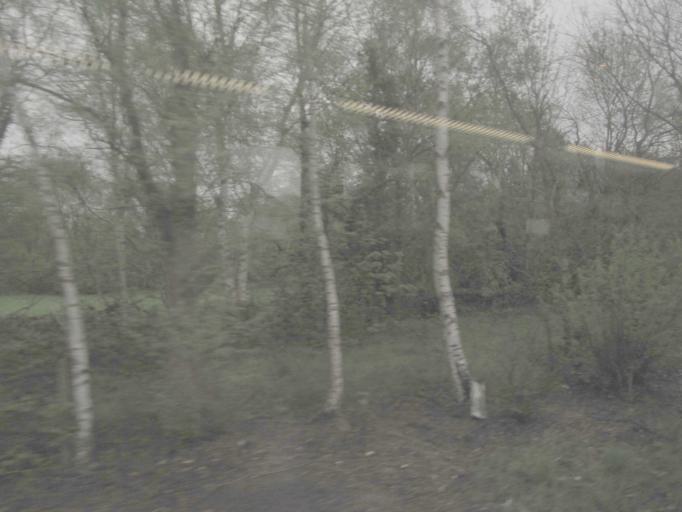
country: GB
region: England
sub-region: Bracknell Forest
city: Sandhurst
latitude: 51.3295
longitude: -0.7745
